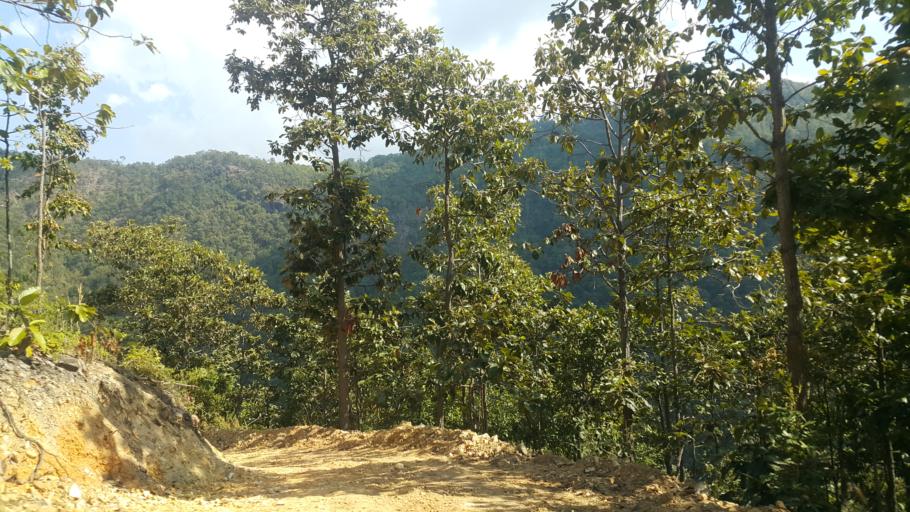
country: TH
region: Lamphun
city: Ban Thi
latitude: 18.6629
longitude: 99.1984
